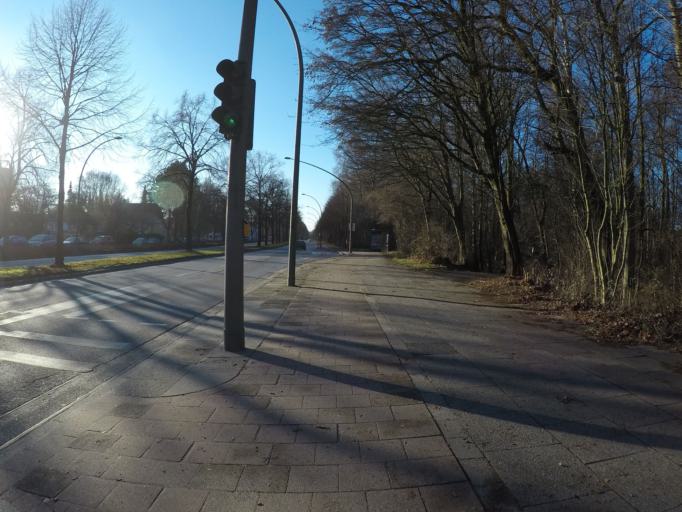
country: DE
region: Hamburg
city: Winterhude
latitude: 53.6102
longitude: 9.9951
